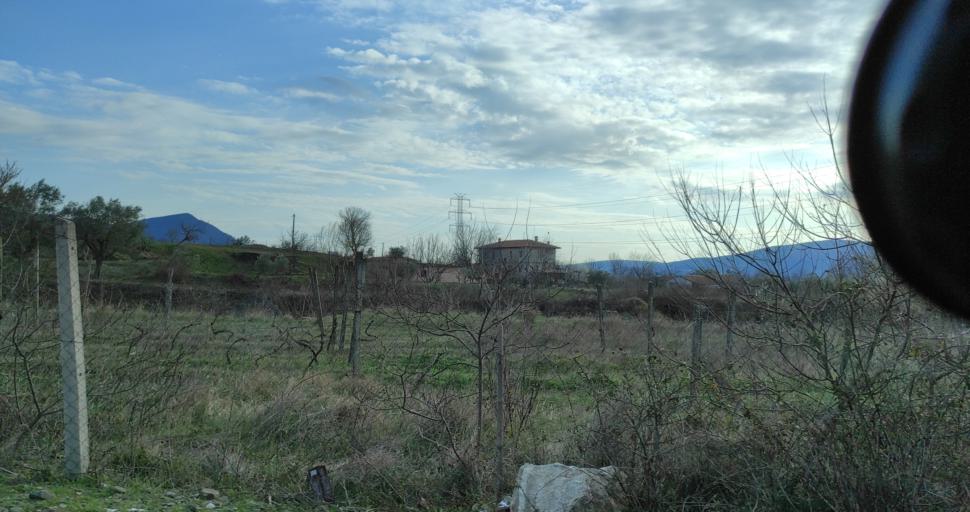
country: AL
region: Lezhe
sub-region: Rrethi i Lezhes
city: Kallmeti i Madh
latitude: 41.8792
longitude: 19.6701
